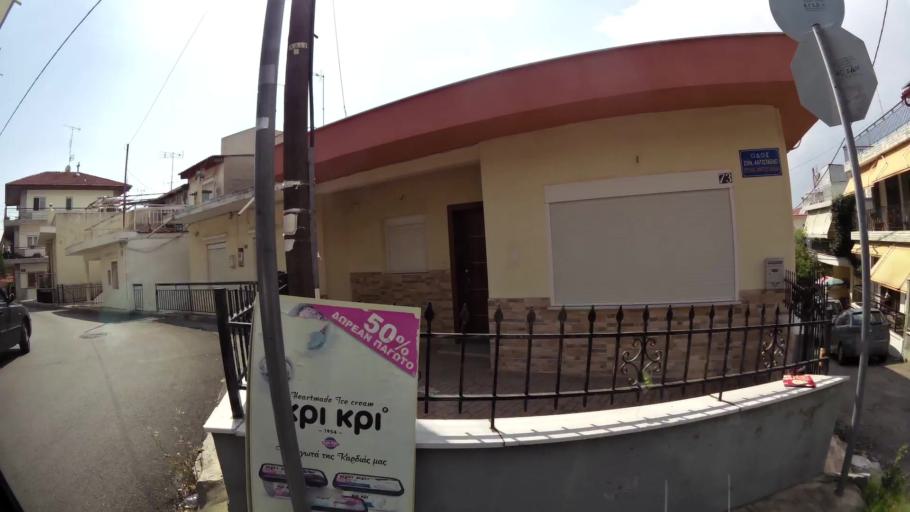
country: GR
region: Central Macedonia
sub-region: Nomos Thessalonikis
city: Polichni
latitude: 40.6641
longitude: 22.9447
